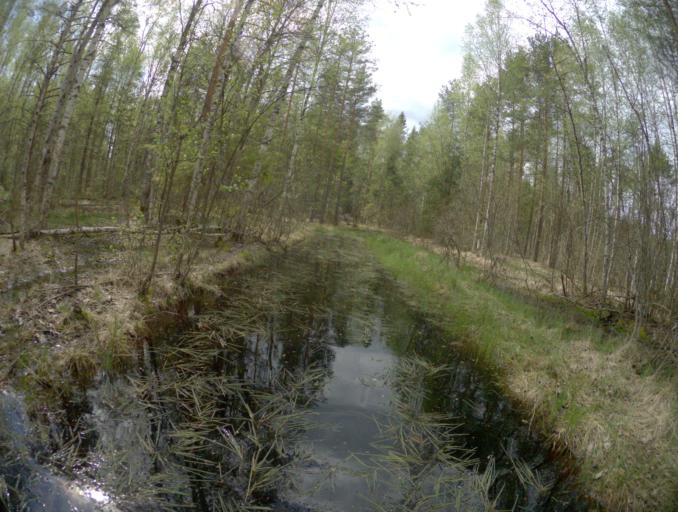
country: RU
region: Vladimir
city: Golovino
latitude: 55.9293
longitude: 40.3868
